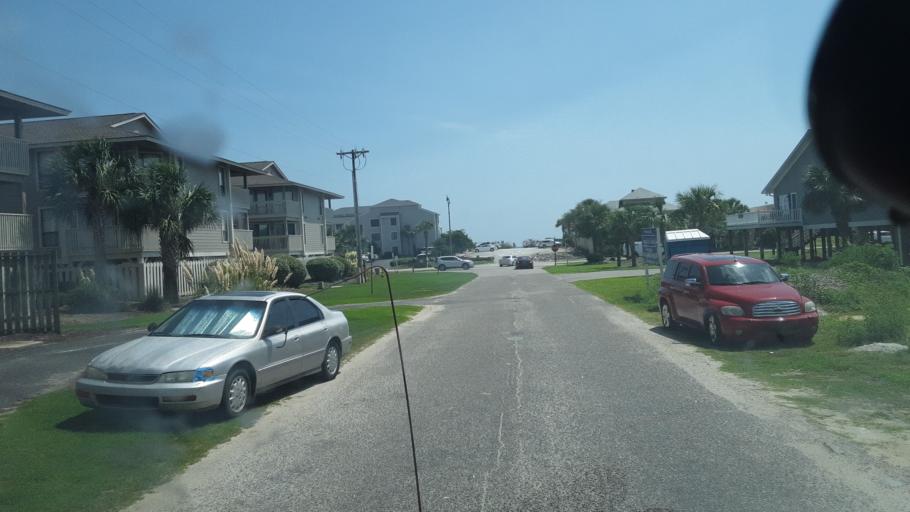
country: US
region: South Carolina
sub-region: Horry County
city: North Myrtle Beach
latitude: 33.8268
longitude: -78.6519
